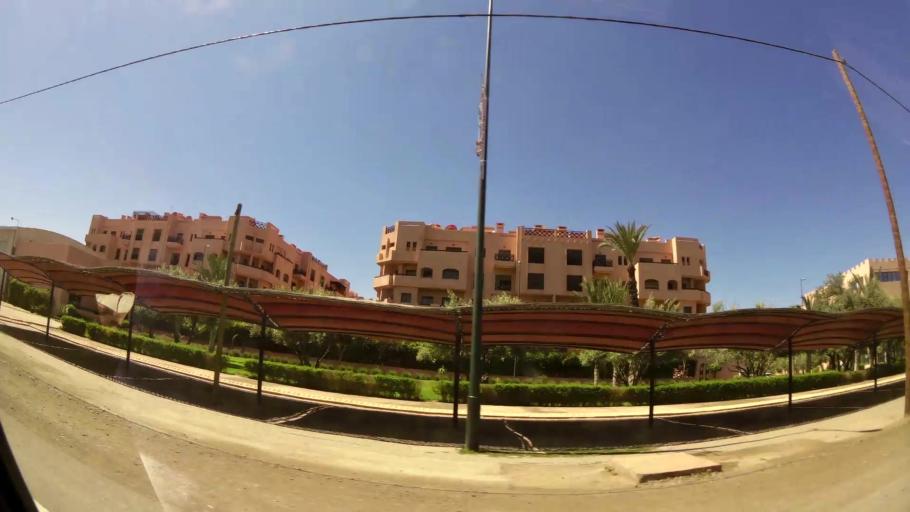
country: MA
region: Marrakech-Tensift-Al Haouz
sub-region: Marrakech
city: Marrakesh
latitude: 31.6631
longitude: -7.9887
